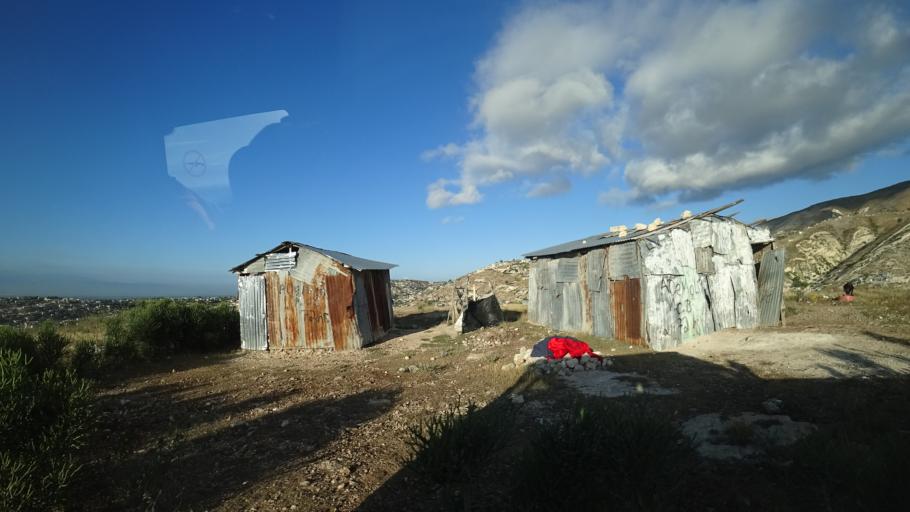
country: HT
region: Ouest
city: Croix des Bouquets
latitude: 18.6651
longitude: -72.2632
